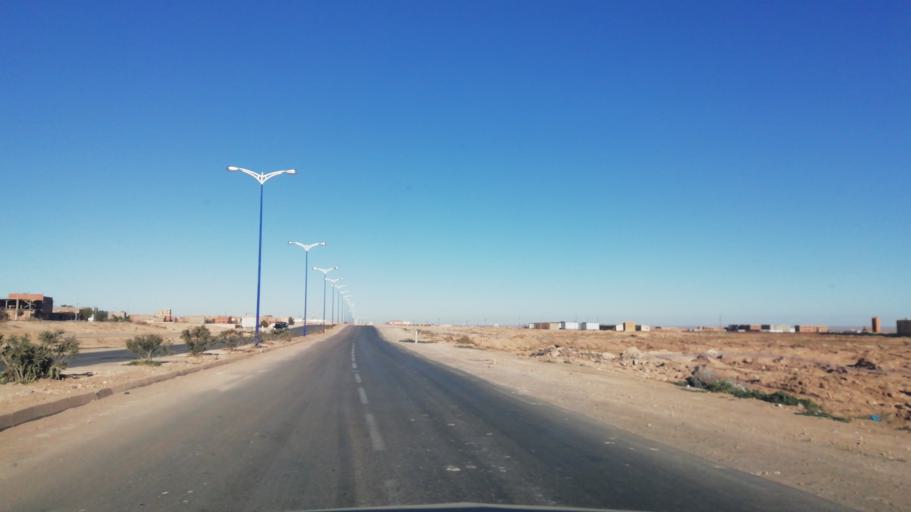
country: DZ
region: Wilaya de Naama
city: Naama
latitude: 33.5354
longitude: -0.2654
